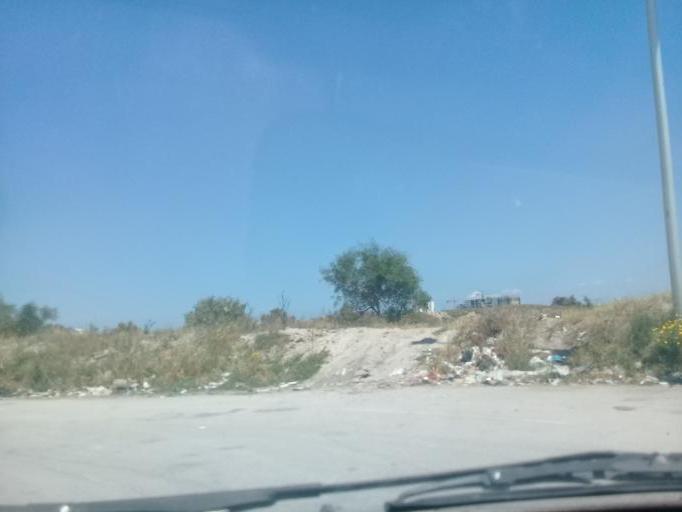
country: TN
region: Tunis
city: La Goulette
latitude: 36.8414
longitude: 10.2838
